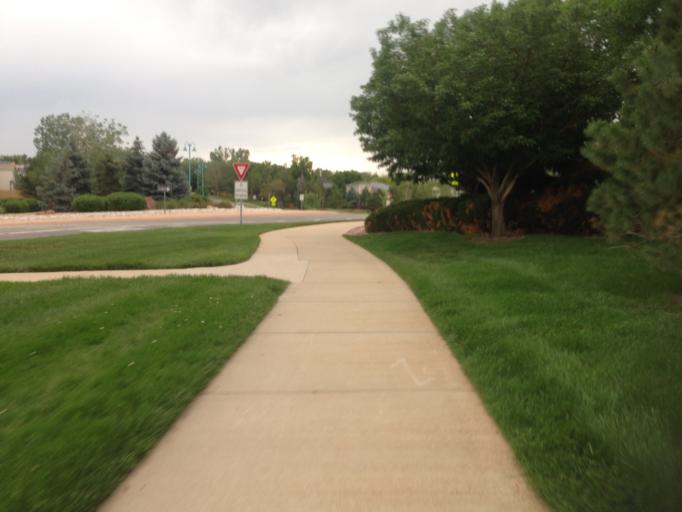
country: US
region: Colorado
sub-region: Boulder County
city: Superior
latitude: 39.9374
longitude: -105.1471
